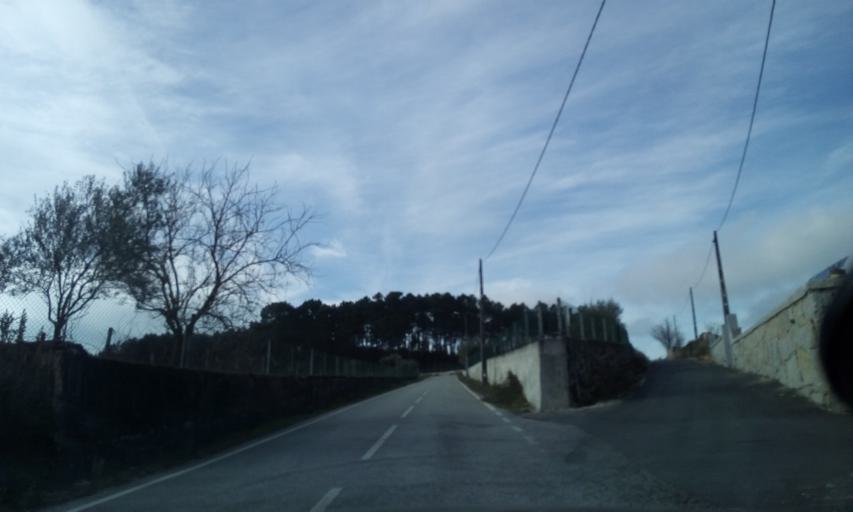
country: PT
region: Guarda
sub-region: Fornos de Algodres
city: Fornos de Algodres
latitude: 40.7009
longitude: -7.5607
